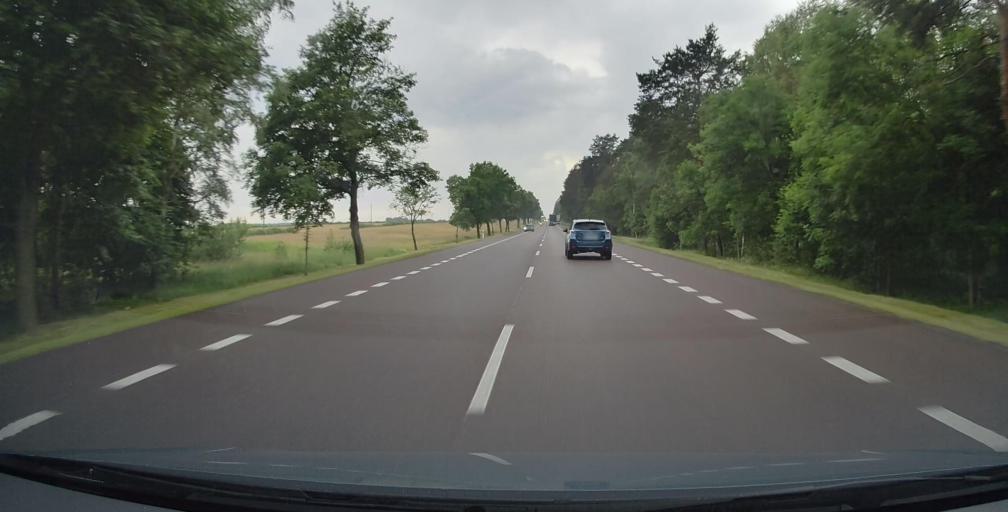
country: PL
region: Lublin Voivodeship
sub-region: Powiat bialski
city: Lesna Podlaska
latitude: 52.0375
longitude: 22.9738
